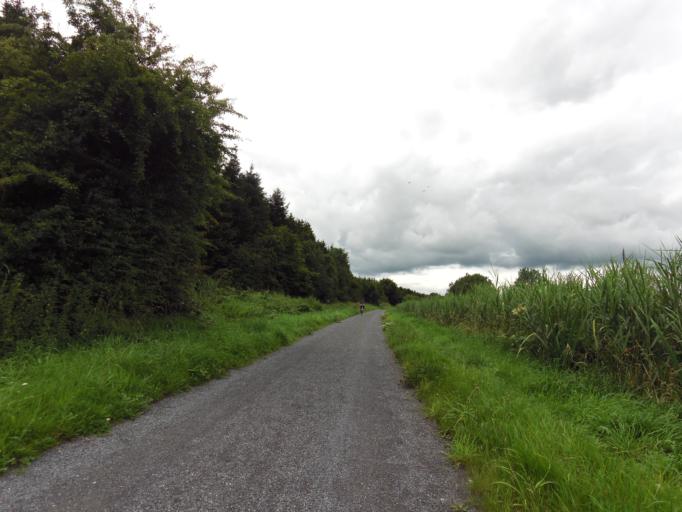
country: IE
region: Leinster
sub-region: An Iarmhi
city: An Muileann gCearr
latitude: 53.5196
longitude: -7.4390
